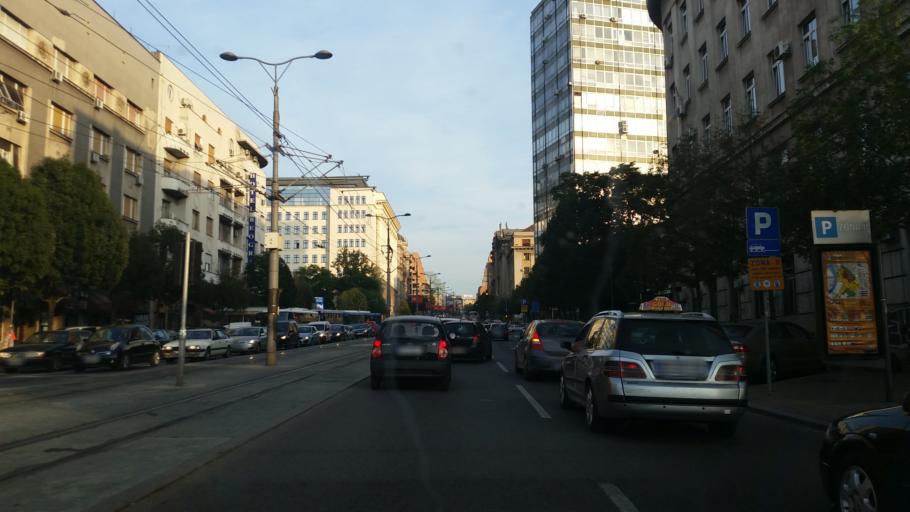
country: RS
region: Central Serbia
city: Belgrade
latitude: 44.8078
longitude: 20.4568
